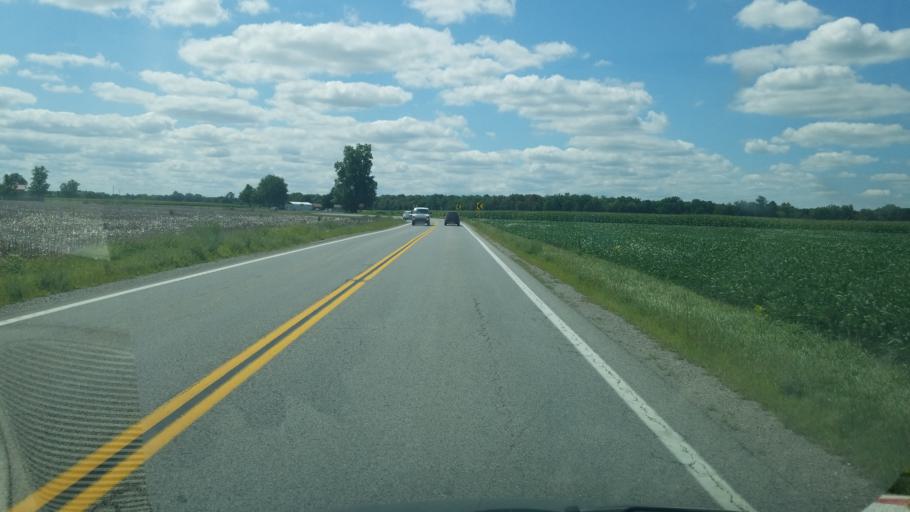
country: US
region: Ohio
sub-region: Fulton County
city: Delta
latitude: 41.6222
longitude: -84.0355
